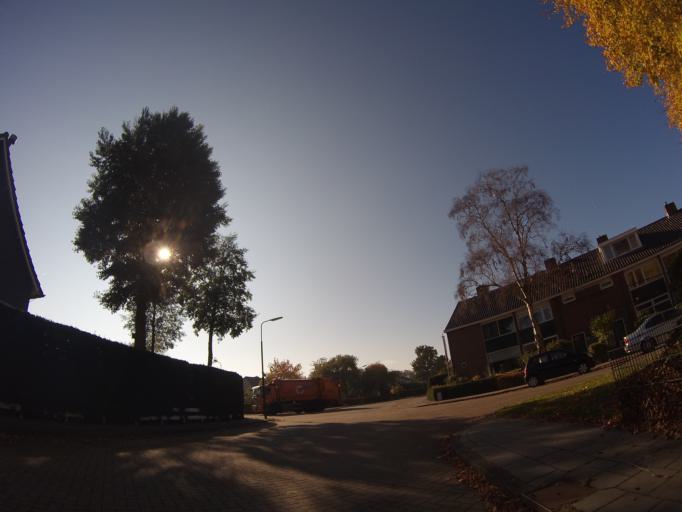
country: NL
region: Utrecht
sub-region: Gemeente Zeist
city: Zeist
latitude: 52.0507
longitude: 5.2385
